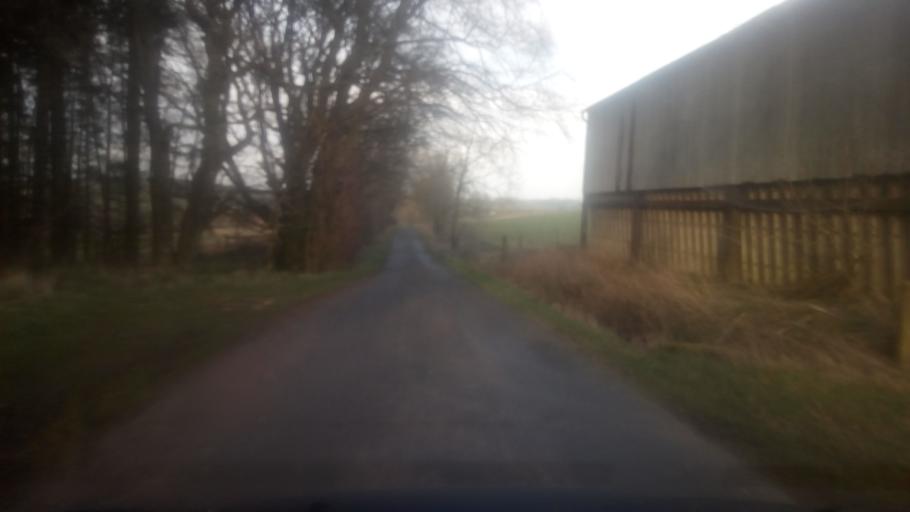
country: GB
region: Scotland
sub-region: The Scottish Borders
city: Jedburgh
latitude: 55.4096
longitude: -2.5191
